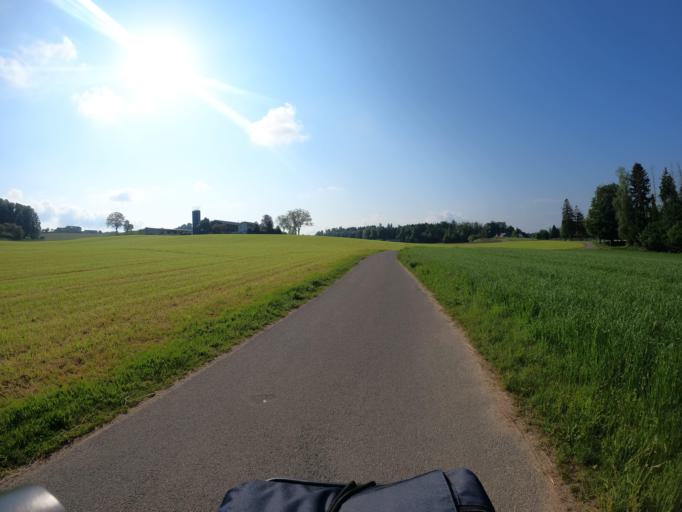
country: CH
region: Zurich
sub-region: Bezirk Affoltern
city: Mettmenstetten
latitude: 47.2396
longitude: 8.4733
